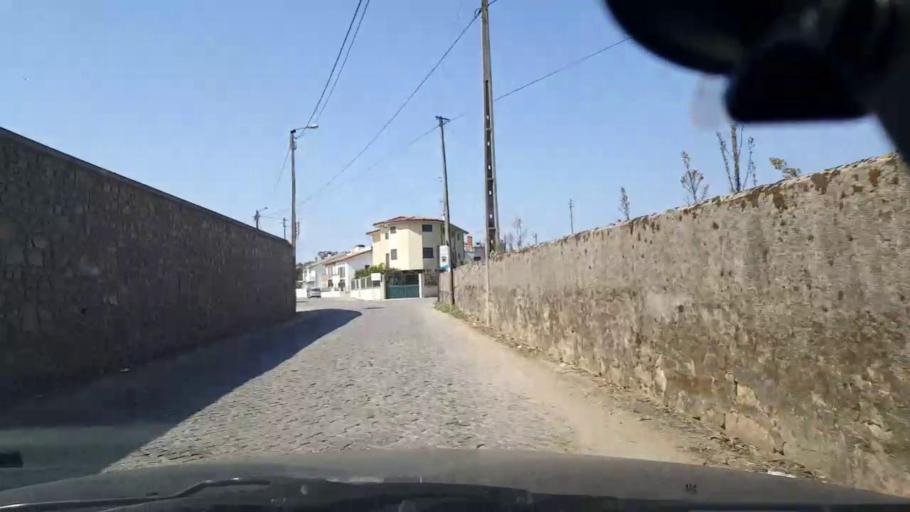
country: PT
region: Porto
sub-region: Povoa de Varzim
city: Pedroso
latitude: 41.3938
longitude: -8.7145
